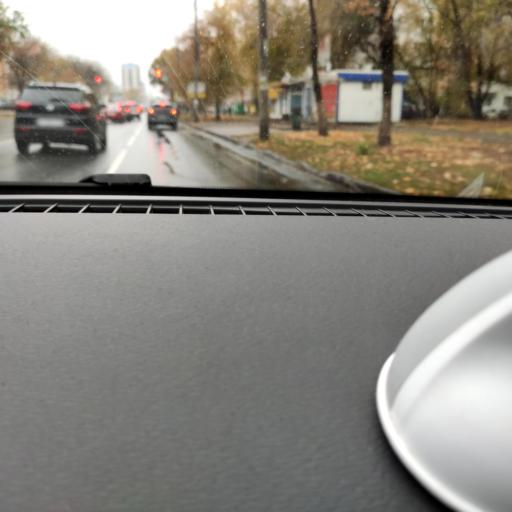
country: RU
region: Samara
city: Samara
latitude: 53.2542
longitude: 50.2331
